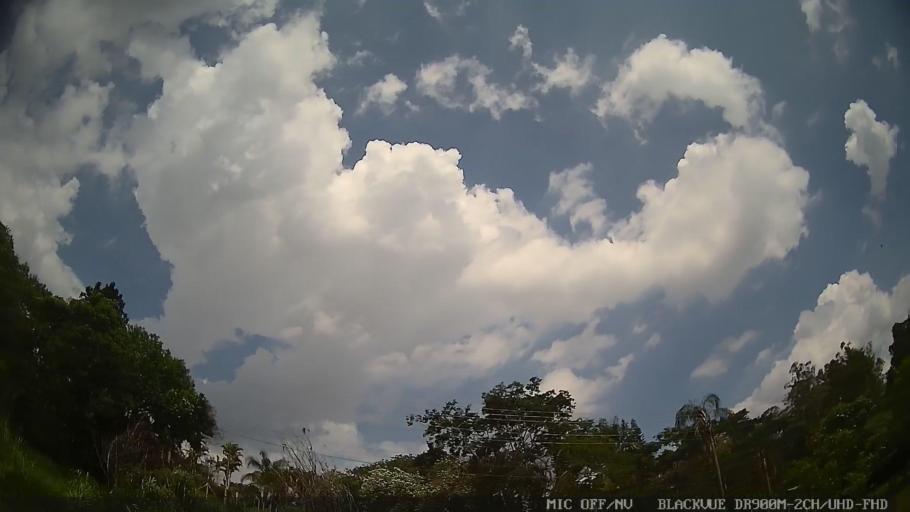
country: BR
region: Sao Paulo
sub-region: Braganca Paulista
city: Braganca Paulista
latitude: -22.9527
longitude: -46.6927
